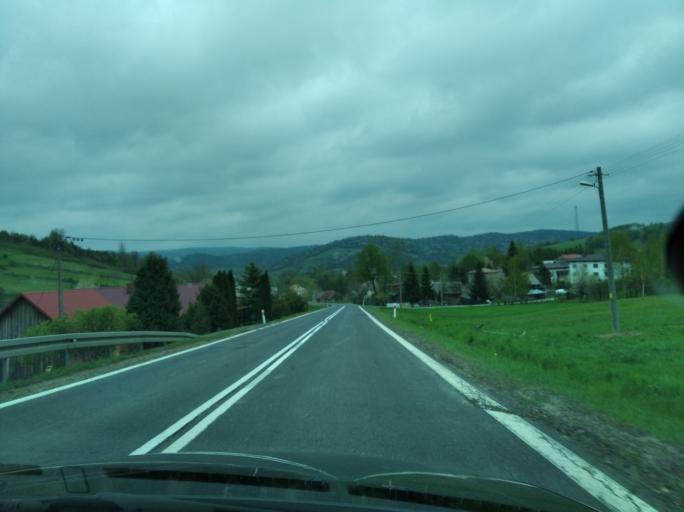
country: PL
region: Subcarpathian Voivodeship
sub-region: Powiat sanocki
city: Tyrawa Woloska
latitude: 49.5695
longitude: 22.3512
